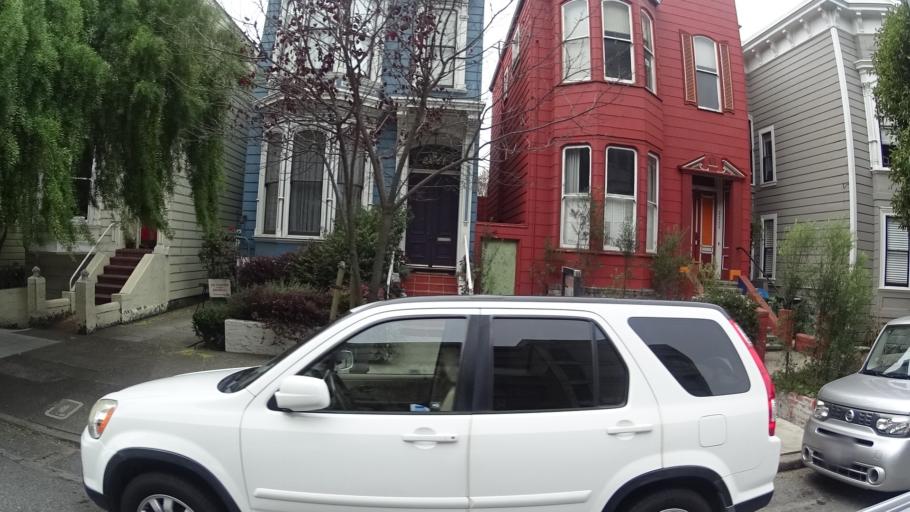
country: US
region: California
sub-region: San Francisco County
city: San Francisco
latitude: 37.7913
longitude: -122.4327
